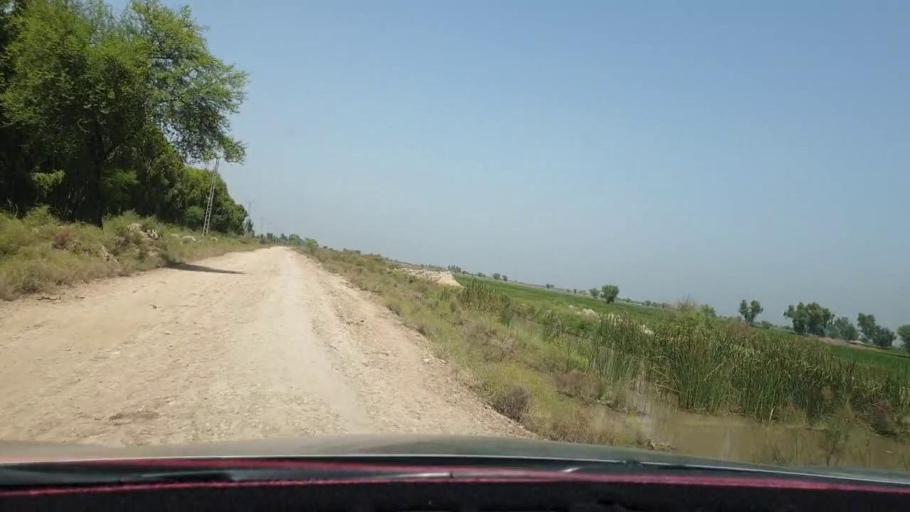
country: PK
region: Sindh
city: Warah
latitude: 27.4159
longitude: 67.6984
